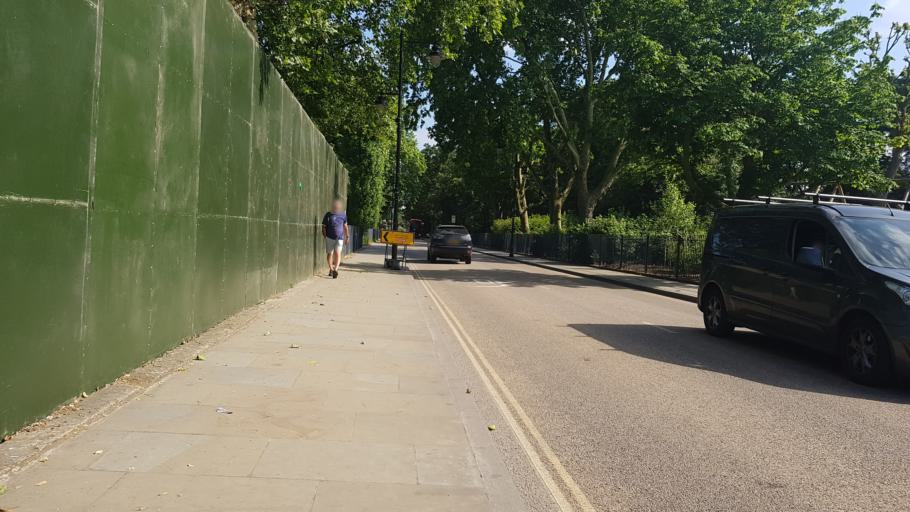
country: GB
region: England
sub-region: Greater London
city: Hackney
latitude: 51.5355
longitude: -0.0427
